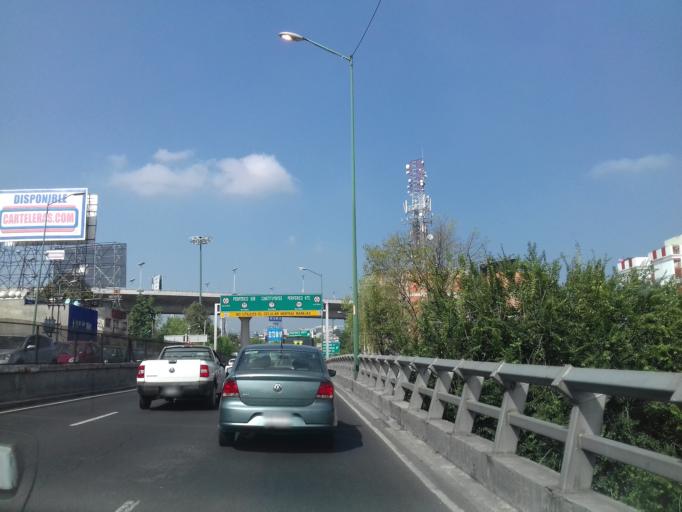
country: MX
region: Mexico City
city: Polanco
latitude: 19.3997
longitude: -99.1889
